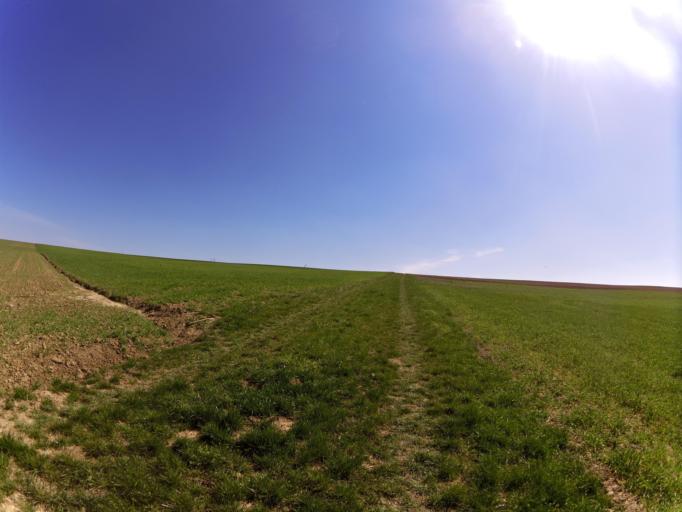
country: DE
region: Bavaria
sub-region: Regierungsbezirk Unterfranken
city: Winterhausen
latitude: 49.6883
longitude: 9.9955
